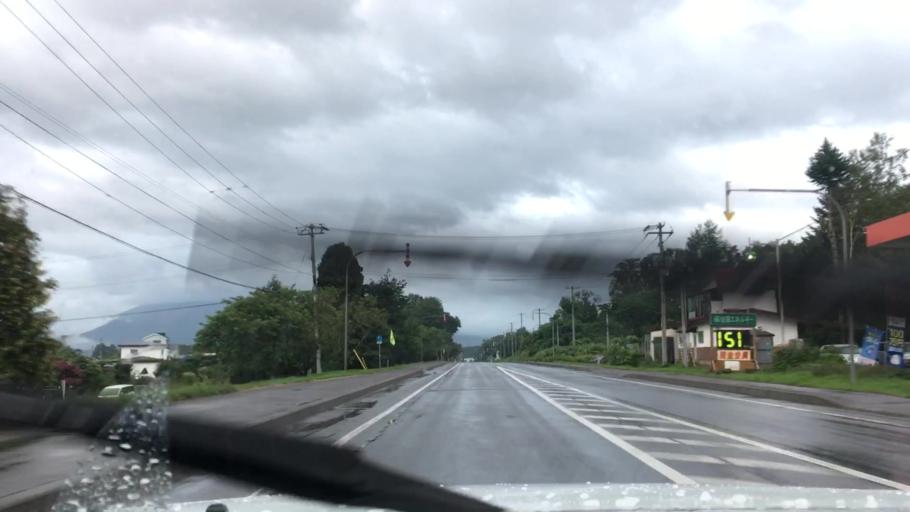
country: JP
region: Hokkaido
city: Nanae
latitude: 42.1111
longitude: 140.5492
